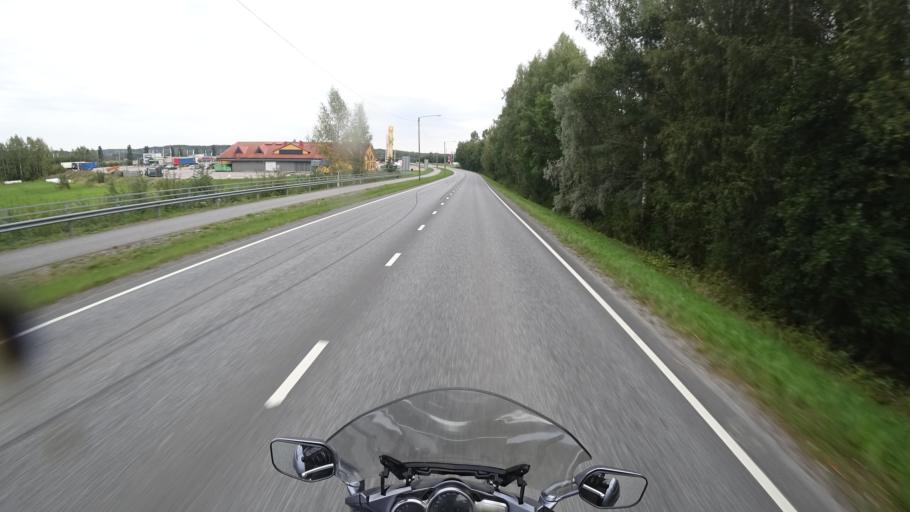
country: FI
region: Uusimaa
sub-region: Raaseporin
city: Karis
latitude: 60.0562
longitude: 23.6449
